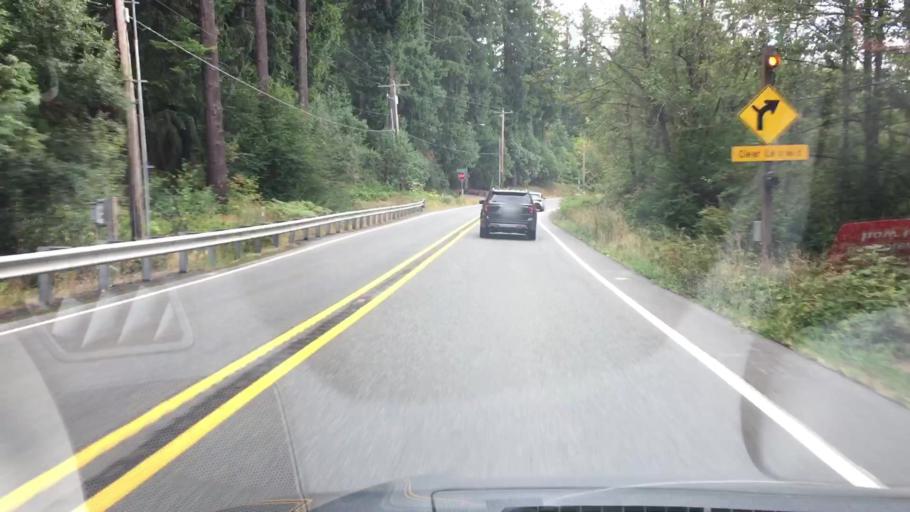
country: US
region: Washington
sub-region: Pierce County
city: Eatonville
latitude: 46.9272
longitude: -122.2814
